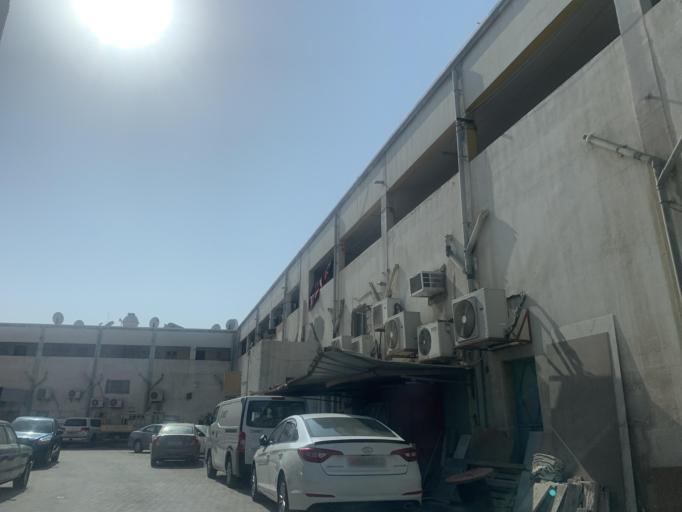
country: BH
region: Central Governorate
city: Madinat Hamad
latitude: 26.1426
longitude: 50.4920
